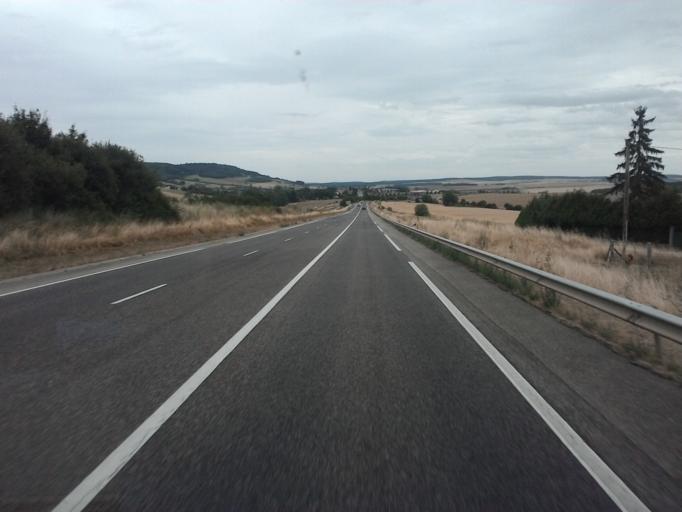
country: FR
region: Lorraine
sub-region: Departement de Meurthe-et-Moselle
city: Bainville-sur-Madon
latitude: 48.5793
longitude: 6.0365
